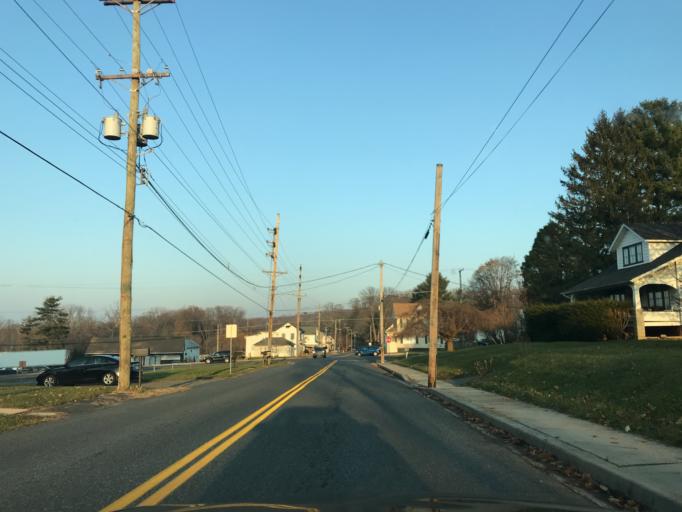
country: US
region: Pennsylvania
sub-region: York County
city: Susquehanna Trails
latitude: 39.7087
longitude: -76.3469
